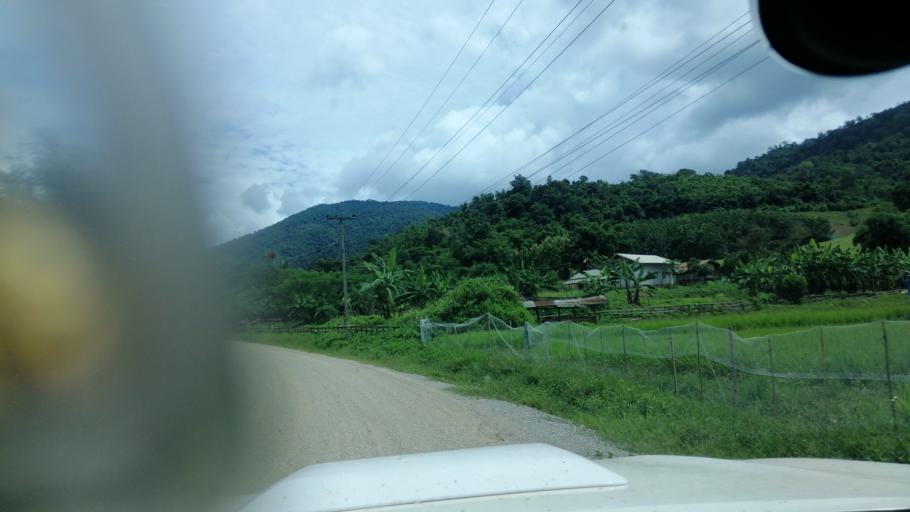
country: TH
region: Phayao
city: Phu Sang
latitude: 19.6840
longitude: 100.5020
